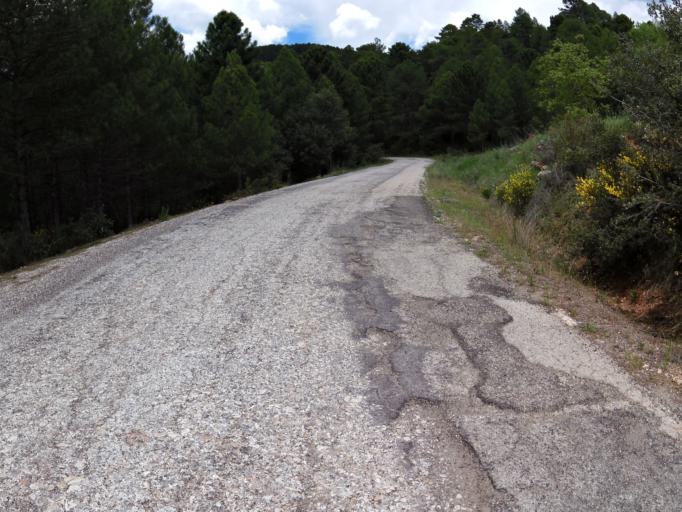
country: ES
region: Castille-La Mancha
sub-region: Provincia de Albacete
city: Paterna del Madera
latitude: 38.5794
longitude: -2.3432
